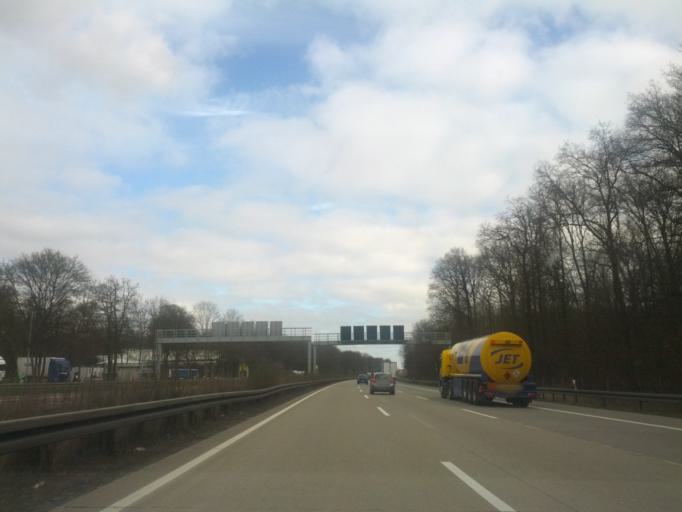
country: DE
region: Lower Saxony
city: Laatzen
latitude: 52.3371
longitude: 9.8652
